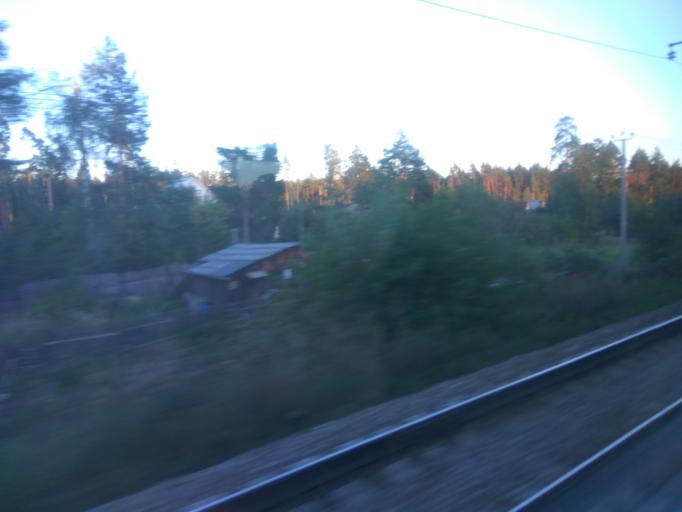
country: RU
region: Moskovskaya
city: Fryazevo
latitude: 55.7471
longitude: 38.4783
